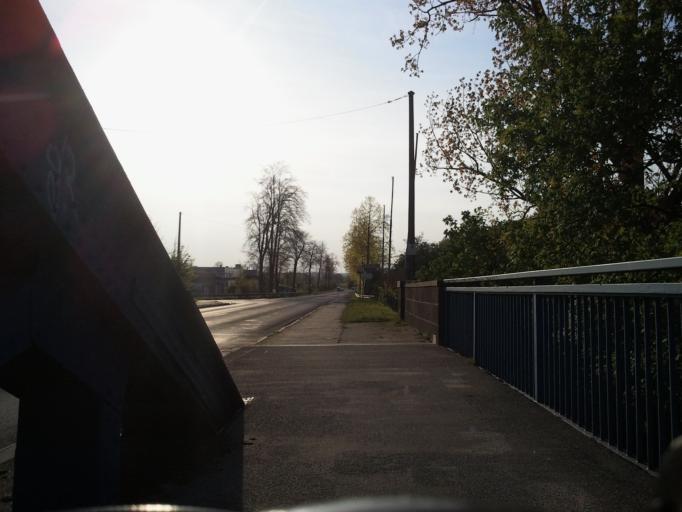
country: DE
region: Lower Saxony
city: Nienburg
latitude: 52.6437
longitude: 9.2029
